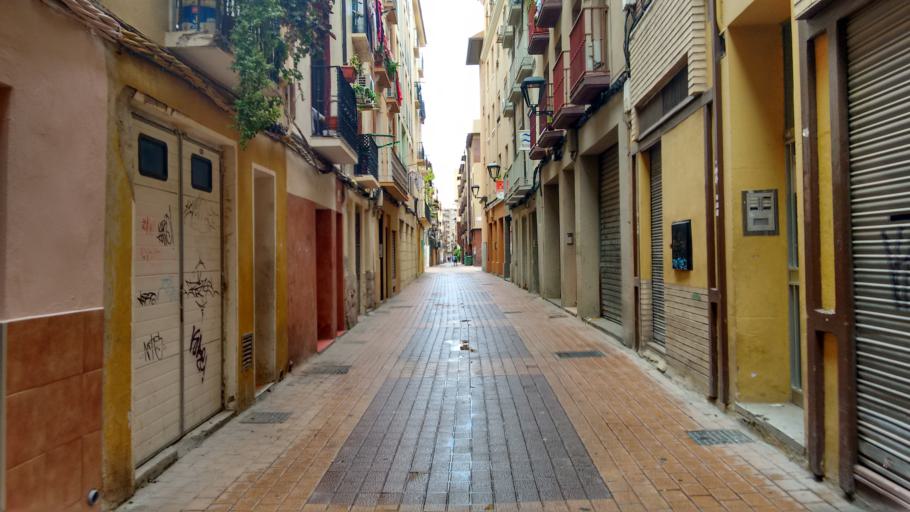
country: ES
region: Aragon
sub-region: Provincia de Zaragoza
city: Zaragoza
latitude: 41.6565
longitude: -0.8846
